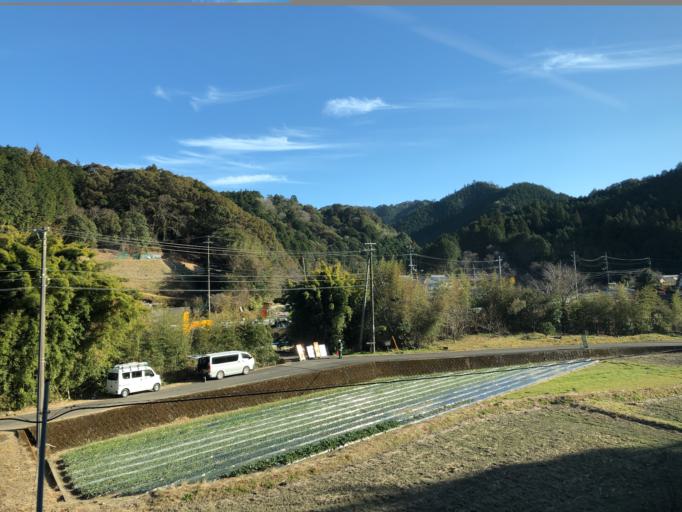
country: JP
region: Kochi
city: Nakamura
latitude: 33.1230
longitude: 133.1192
